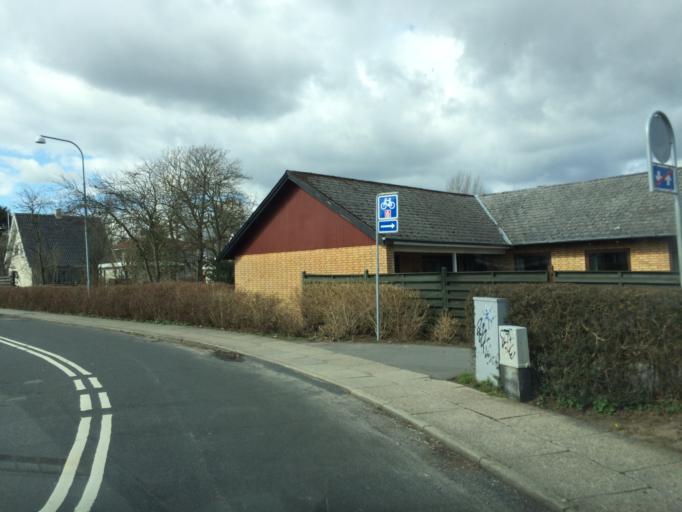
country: DK
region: South Denmark
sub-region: Nordfyns Kommune
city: Sonderso
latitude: 55.4176
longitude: 10.2762
